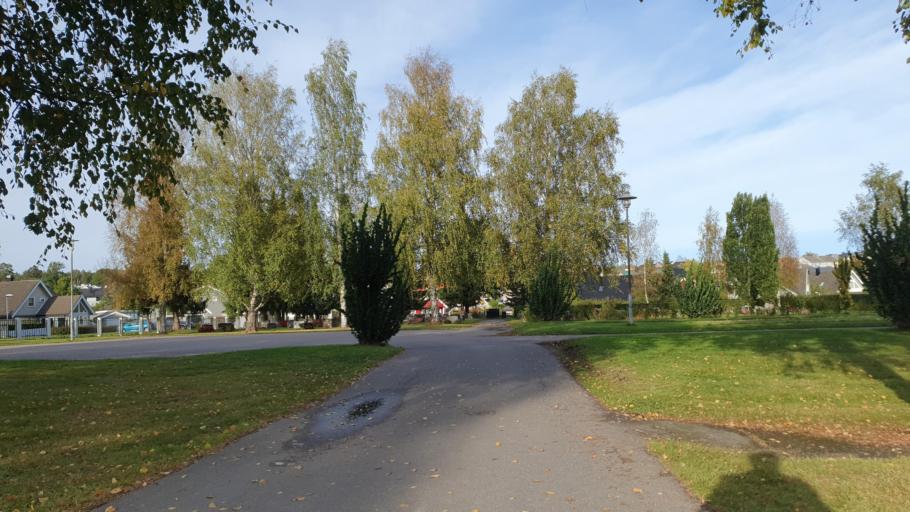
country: NO
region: Vestfold
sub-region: Tonsberg
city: Tonsberg
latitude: 59.2749
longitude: 10.4201
